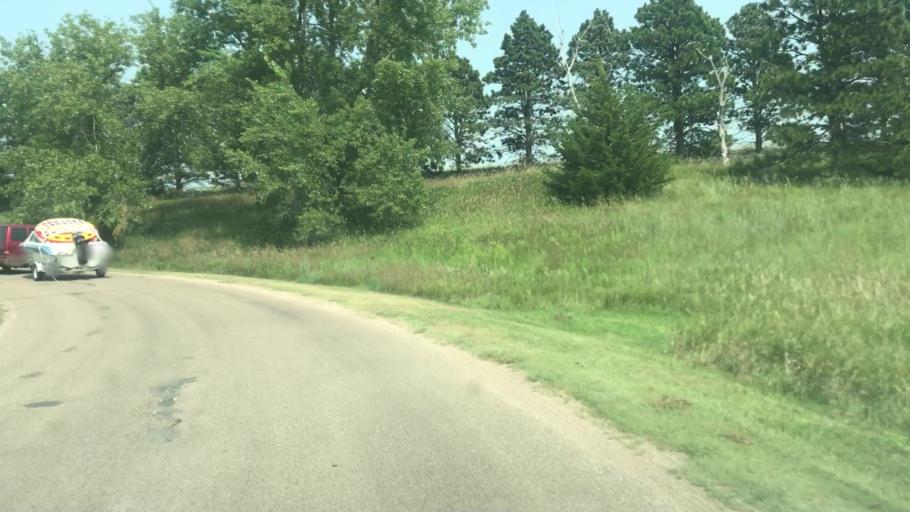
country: US
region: Nebraska
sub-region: Sherman County
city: Loup City
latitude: 41.2871
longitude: -98.8935
